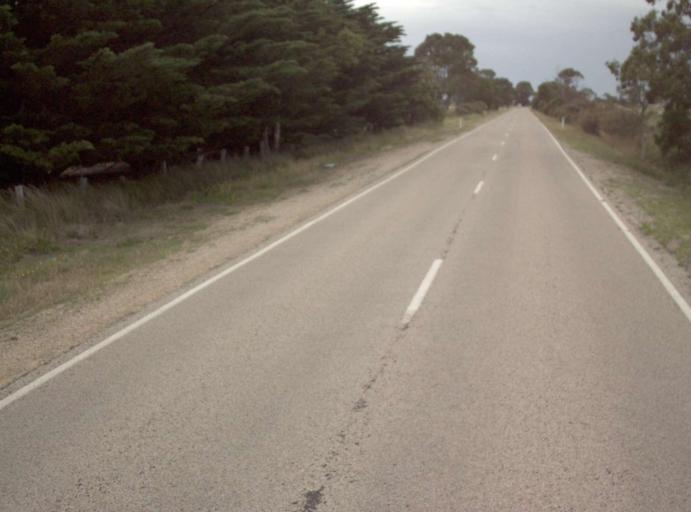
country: AU
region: Victoria
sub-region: East Gippsland
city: Bairnsdale
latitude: -37.8882
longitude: 147.5572
